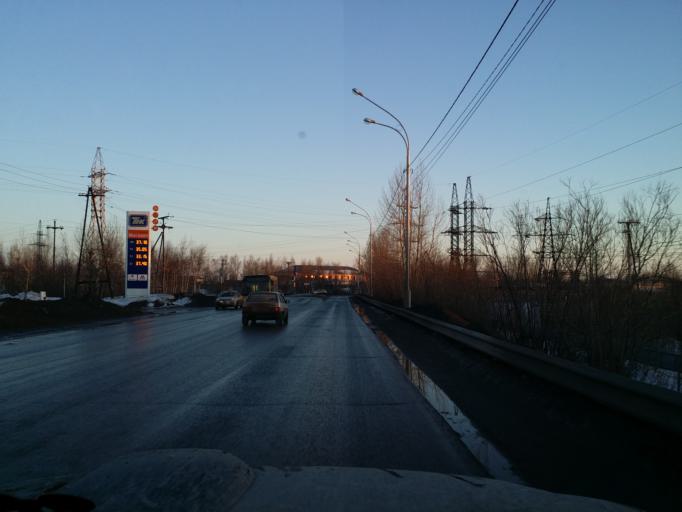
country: RU
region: Khanty-Mansiyskiy Avtonomnyy Okrug
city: Nizhnevartovsk
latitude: 60.9283
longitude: 76.5314
